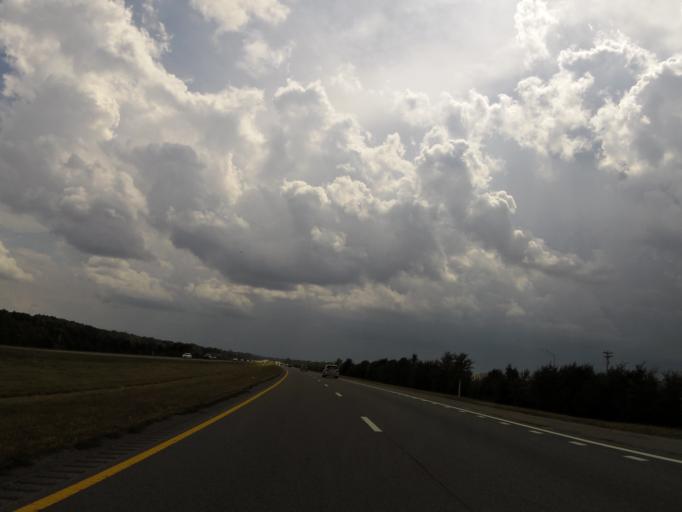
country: US
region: Tennessee
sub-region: Wilson County
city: Rural Hill
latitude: 36.1238
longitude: -86.4063
